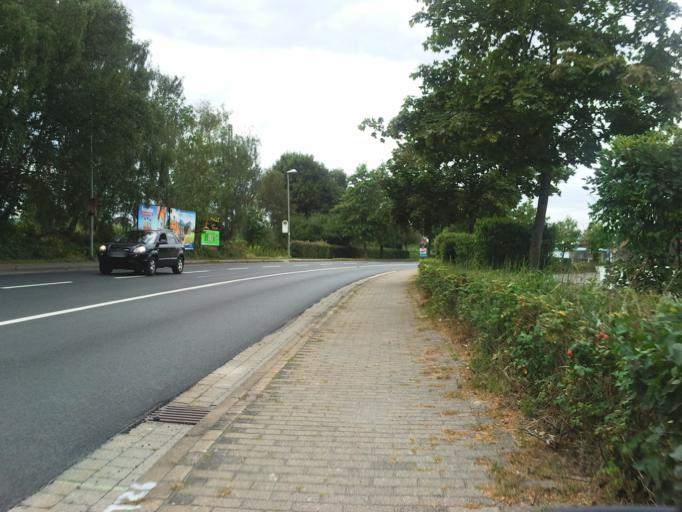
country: DE
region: Lower Saxony
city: Nienburg
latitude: 52.6417
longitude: 9.2243
